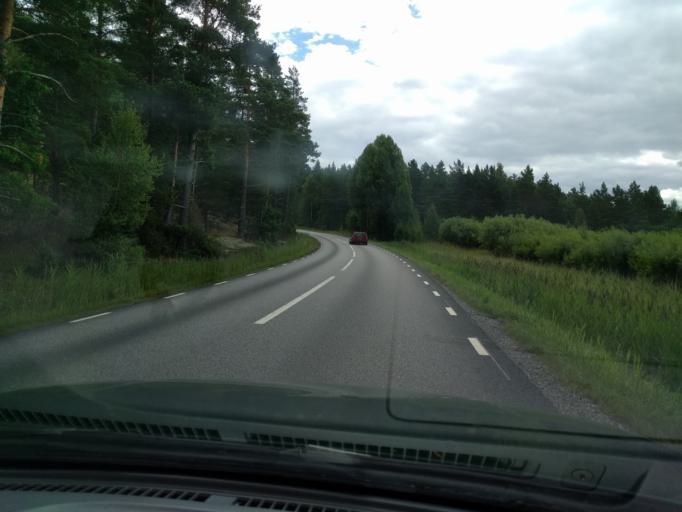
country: SE
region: Soedermanland
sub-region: Nykopings Kommun
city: Svalsta
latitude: 58.5304
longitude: 16.7490
